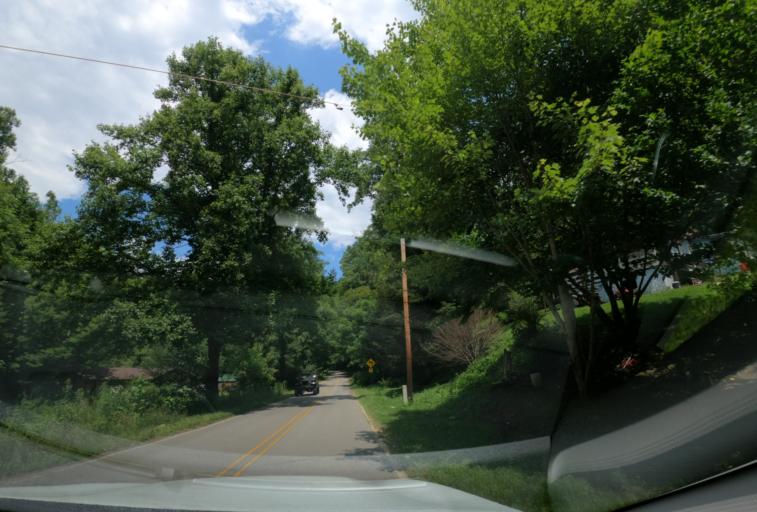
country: US
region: North Carolina
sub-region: Haywood County
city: Waynesville
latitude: 35.4175
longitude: -82.9062
